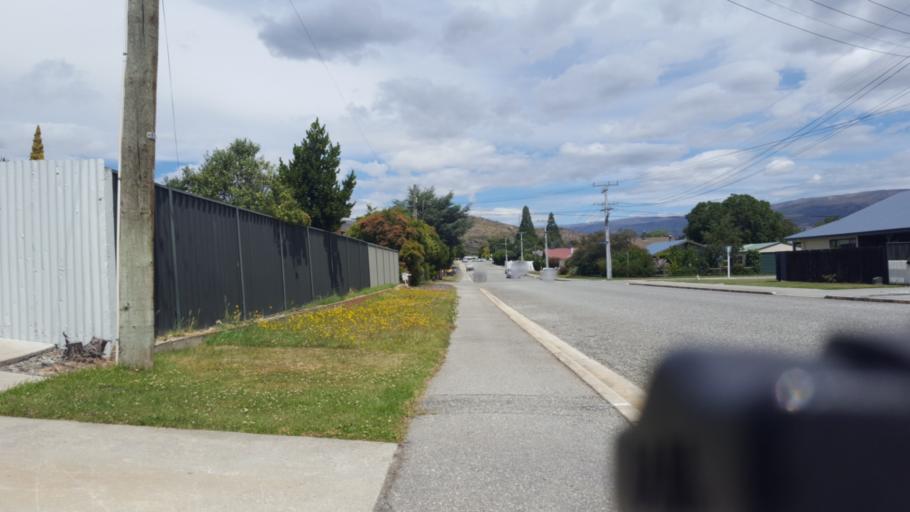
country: NZ
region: Otago
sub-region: Queenstown-Lakes District
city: Wanaka
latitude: -45.0441
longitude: 169.2114
